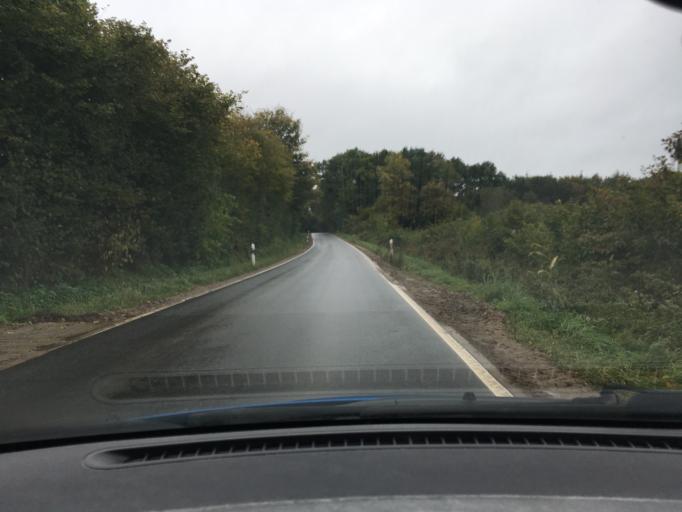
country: DE
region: Schleswig-Holstein
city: Nehmten
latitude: 54.0781
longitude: 10.3968
